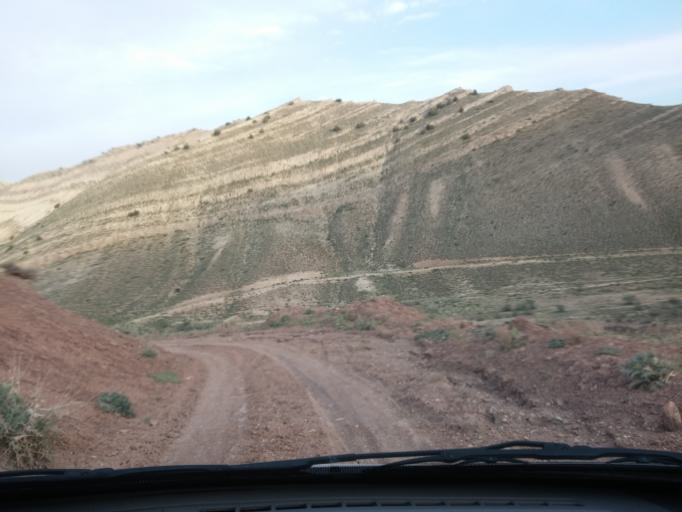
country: IR
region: Semnan
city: Istgah-e Rah Ahan-e Garmsar
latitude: 35.4743
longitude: 52.2910
